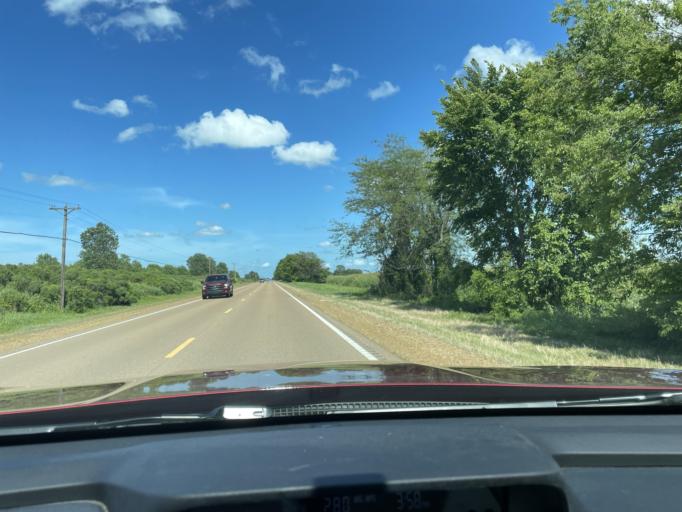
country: US
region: Mississippi
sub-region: Humphreys County
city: Belzoni
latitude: 33.1837
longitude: -90.5879
